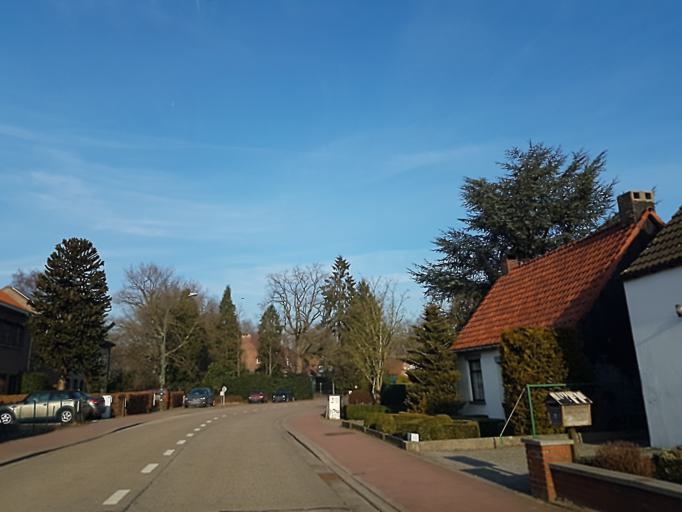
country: BE
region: Flanders
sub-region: Provincie Antwerpen
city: Schilde
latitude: 51.2657
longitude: 4.5521
